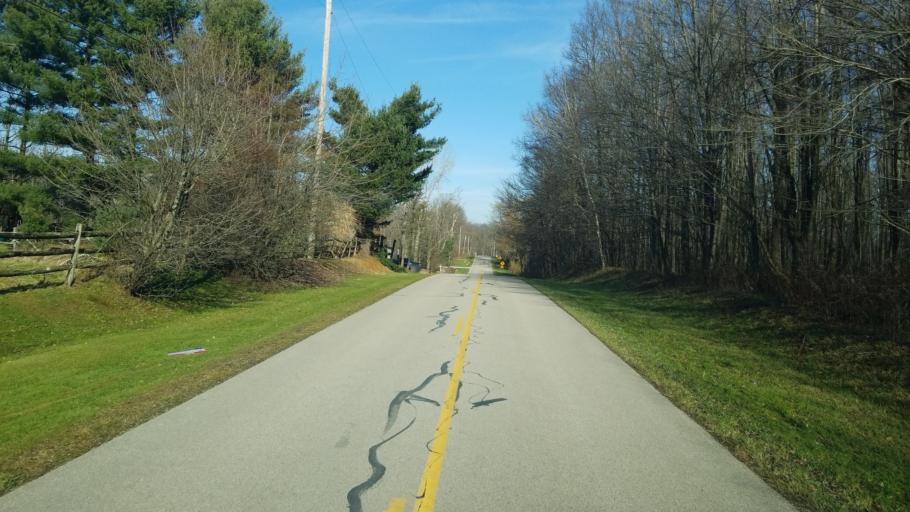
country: US
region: Ohio
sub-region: Ashtabula County
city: Jefferson
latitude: 41.7579
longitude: -80.7898
